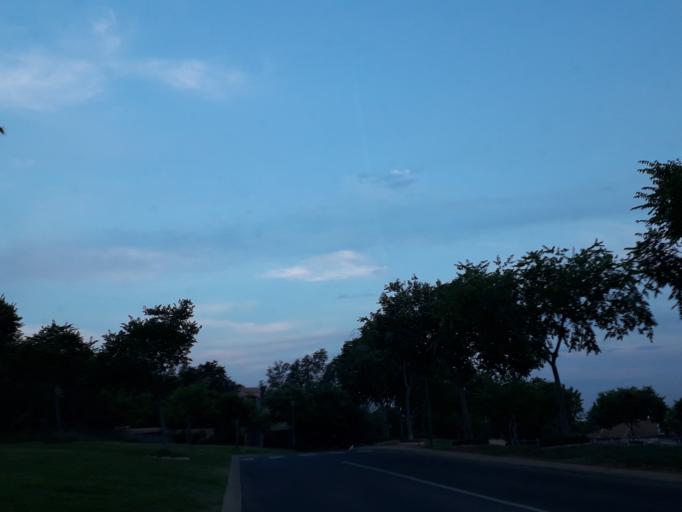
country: ZA
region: Gauteng
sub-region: City of Johannesburg Metropolitan Municipality
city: Diepsloot
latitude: -25.9830
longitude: 28.0004
